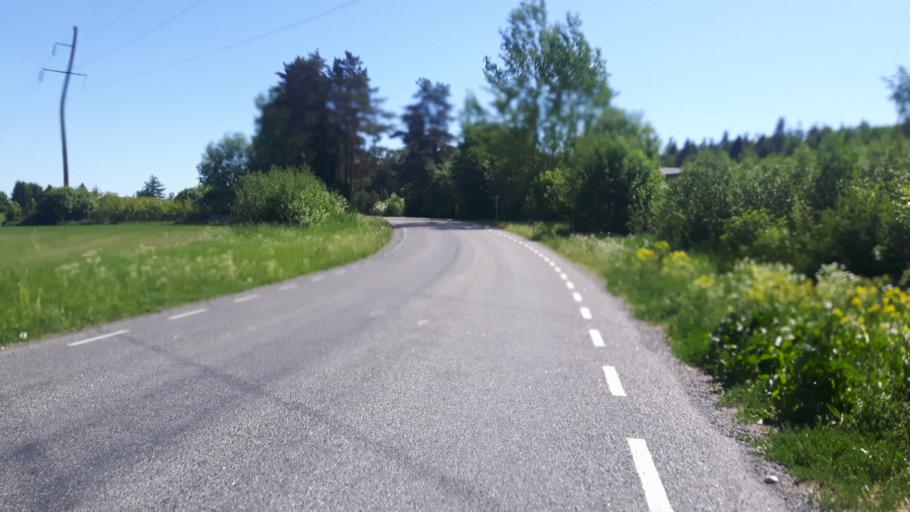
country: EE
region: Raplamaa
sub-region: Kohila vald
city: Kohila
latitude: 59.1779
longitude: 24.7275
